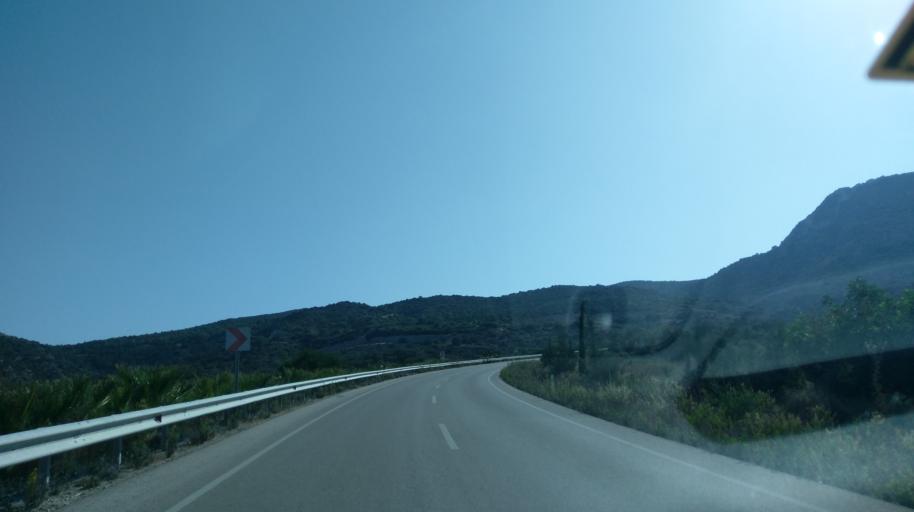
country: CY
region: Ammochostos
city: Trikomo
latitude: 35.4354
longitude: 33.9613
